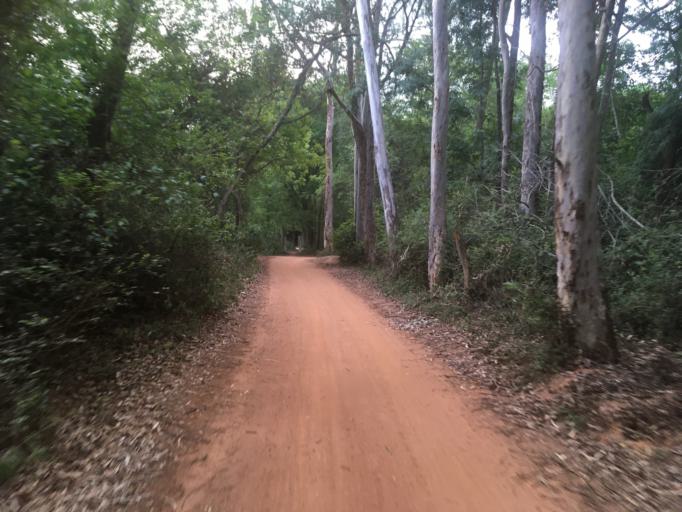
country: IN
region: Tamil Nadu
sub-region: Villupuram
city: Auroville
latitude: 12.0146
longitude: 79.8040
